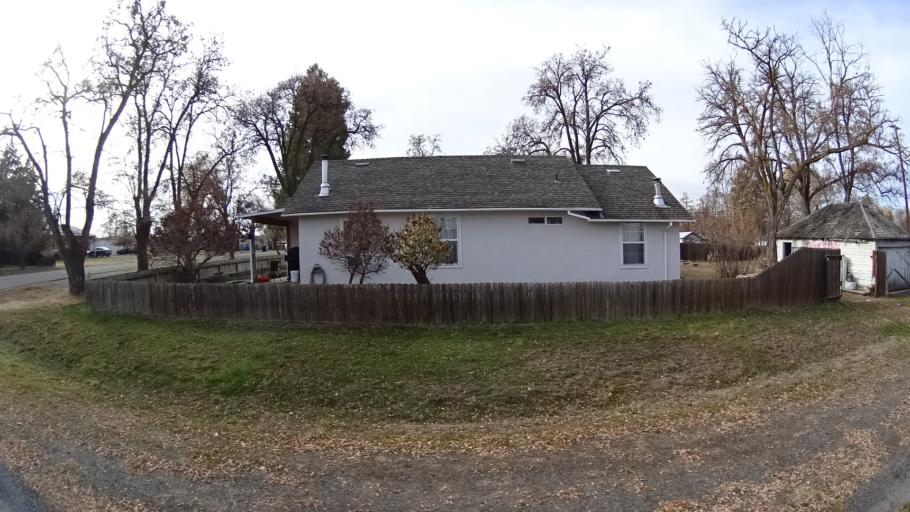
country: US
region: California
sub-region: Siskiyou County
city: Montague
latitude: 41.7312
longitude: -122.5276
